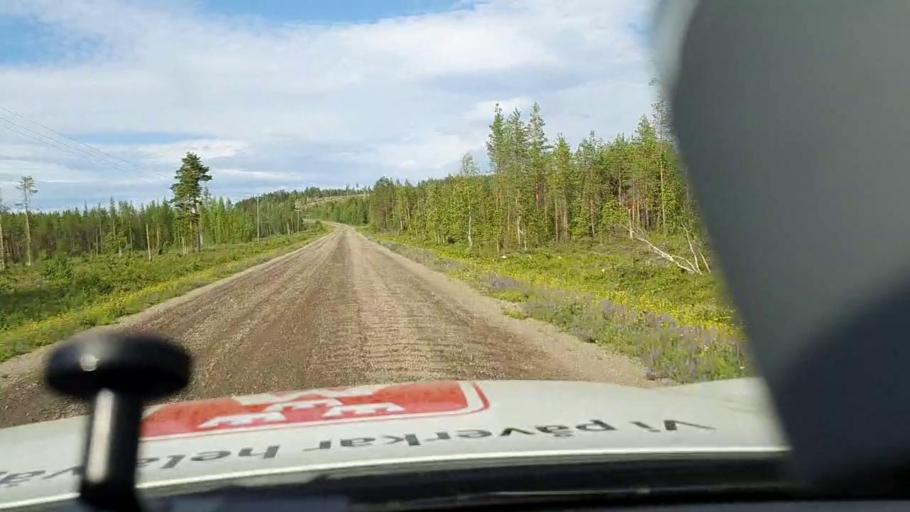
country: SE
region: Norrbotten
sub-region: Alvsbyns Kommun
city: AElvsbyn
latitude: 66.1621
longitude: 21.0503
